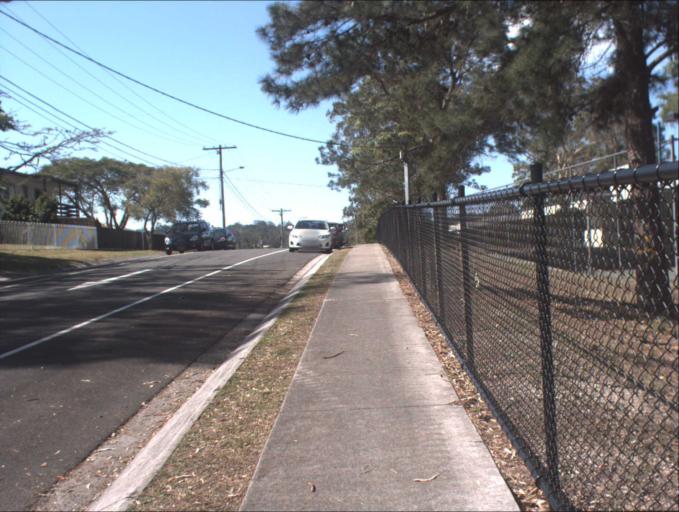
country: AU
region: Queensland
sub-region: Logan
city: Slacks Creek
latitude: -27.6438
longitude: 153.1513
